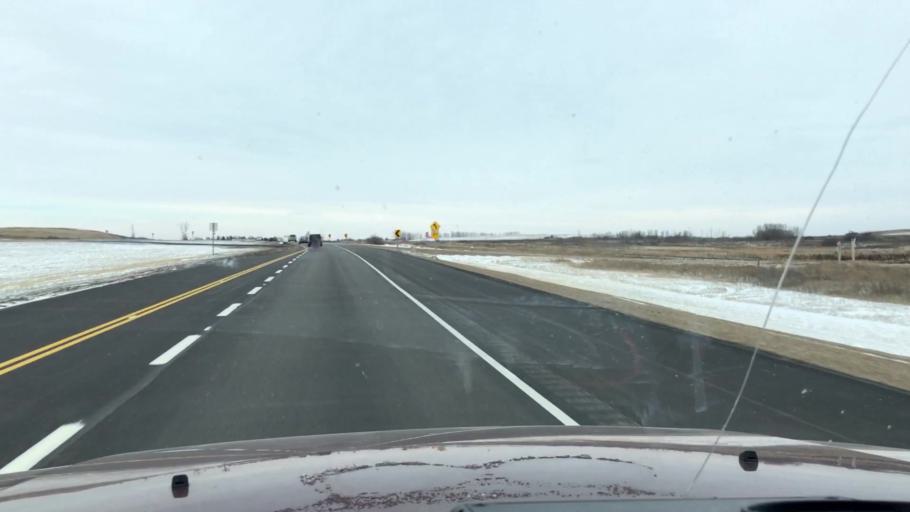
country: CA
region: Saskatchewan
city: Moose Jaw
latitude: 50.8636
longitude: -105.5935
